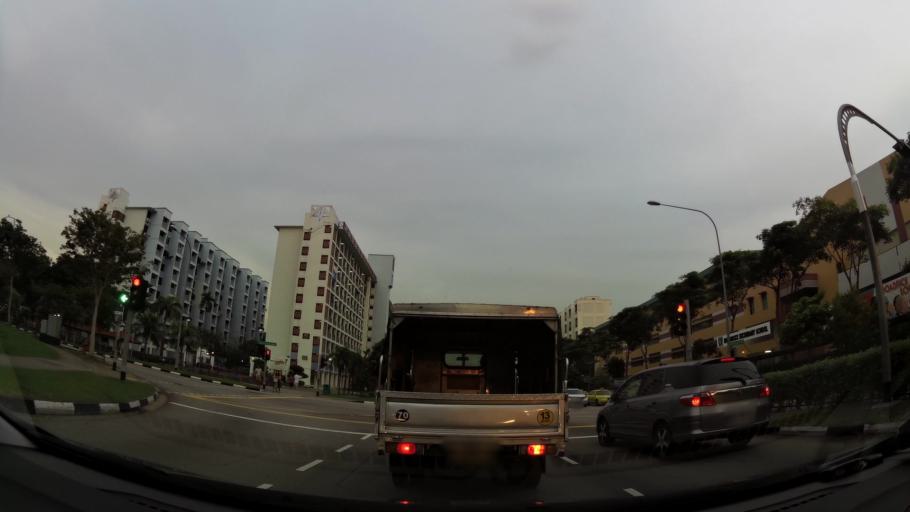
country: SG
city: Singapore
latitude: 1.3080
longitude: 103.8865
